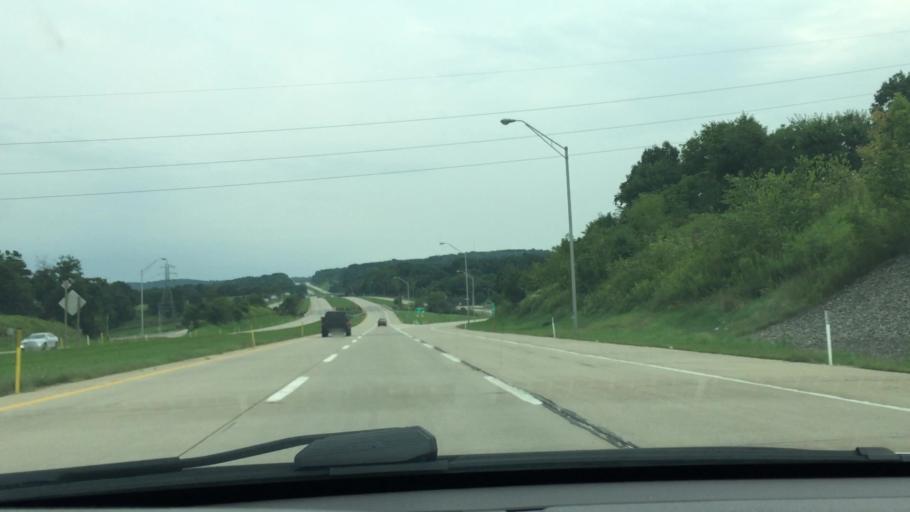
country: US
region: Pennsylvania
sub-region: Lawrence County
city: New Beaver
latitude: 40.9229
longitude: -80.3868
